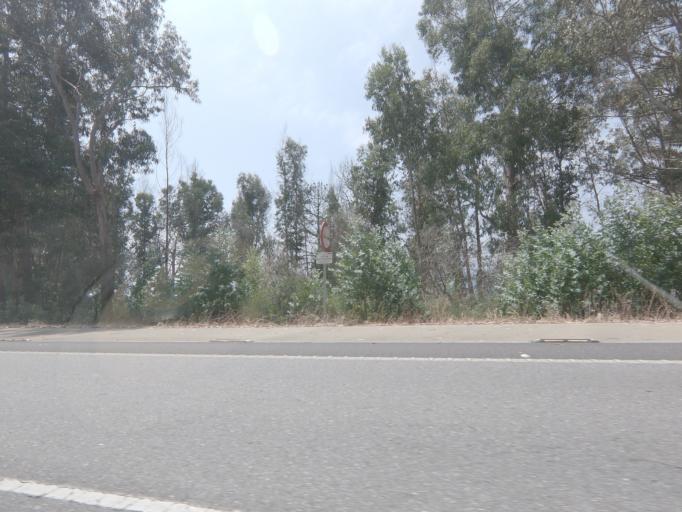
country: ES
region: Galicia
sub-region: Provincia de Pontevedra
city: A Guarda
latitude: 41.9243
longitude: -8.8808
